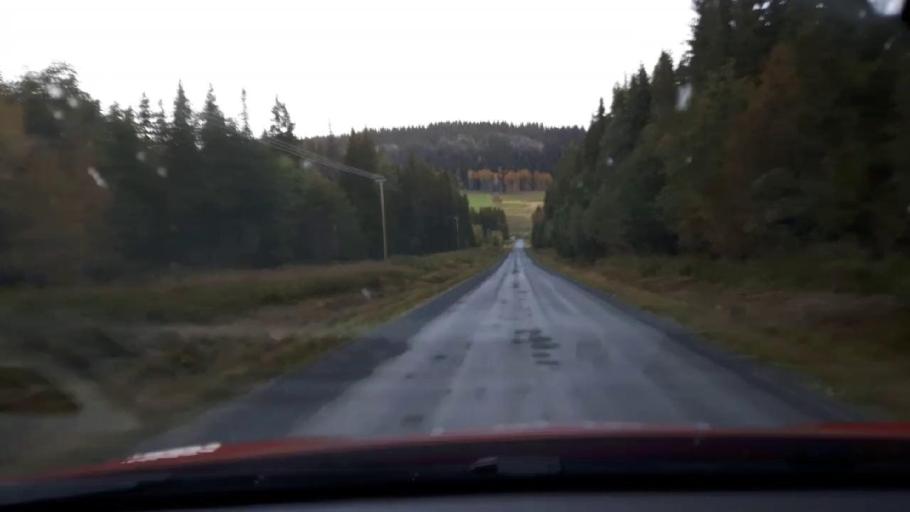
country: SE
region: Jaemtland
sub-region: Krokoms Kommun
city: Krokom
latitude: 63.4840
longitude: 14.2066
